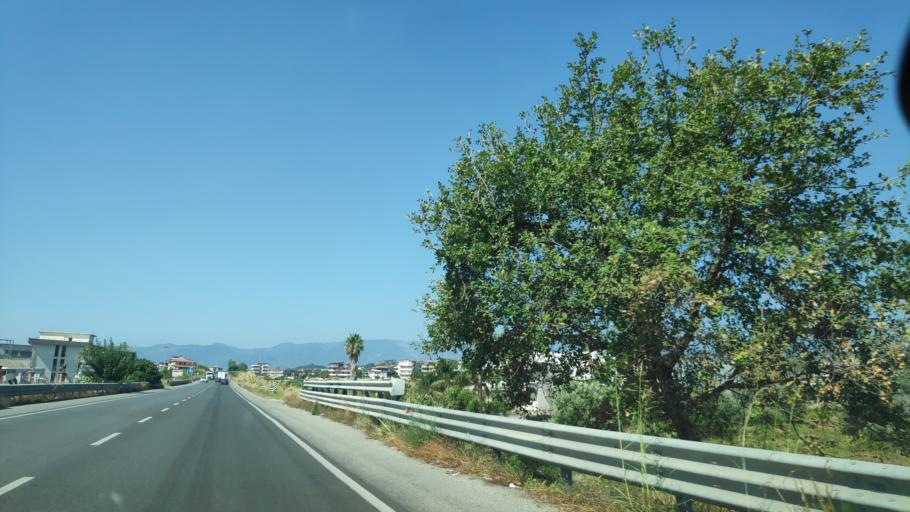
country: IT
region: Calabria
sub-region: Provincia di Reggio Calabria
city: Ardore Marina
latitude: 38.1601
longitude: 16.1881
